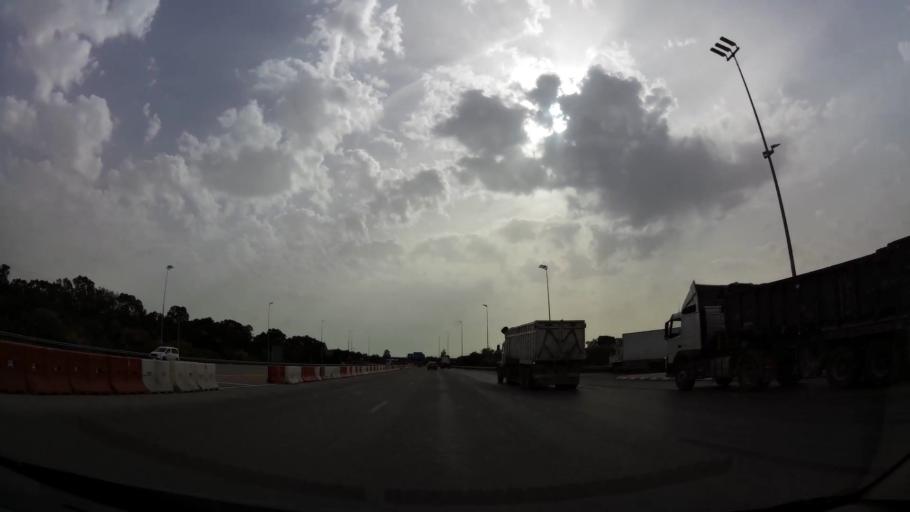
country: MA
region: Tanger-Tetouan
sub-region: Tanger-Assilah
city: Boukhalef
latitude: 35.6776
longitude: -5.9289
